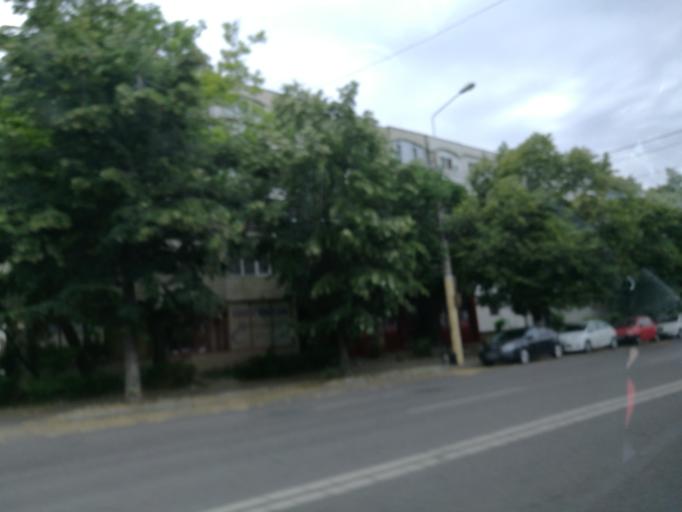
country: RO
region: Constanta
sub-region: Municipiul Constanta
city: Constanta
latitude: 44.1937
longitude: 28.6327
